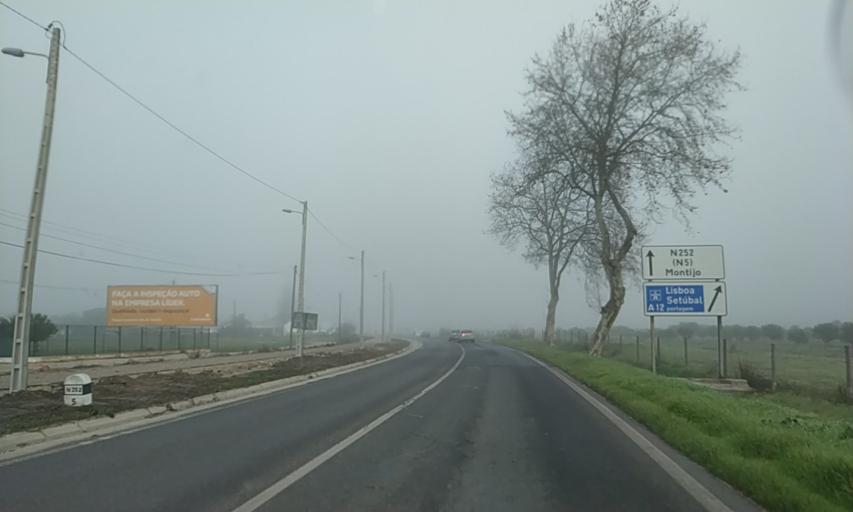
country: PT
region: Setubal
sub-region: Palmela
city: Pinhal Novo
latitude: 38.6461
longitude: -8.9149
